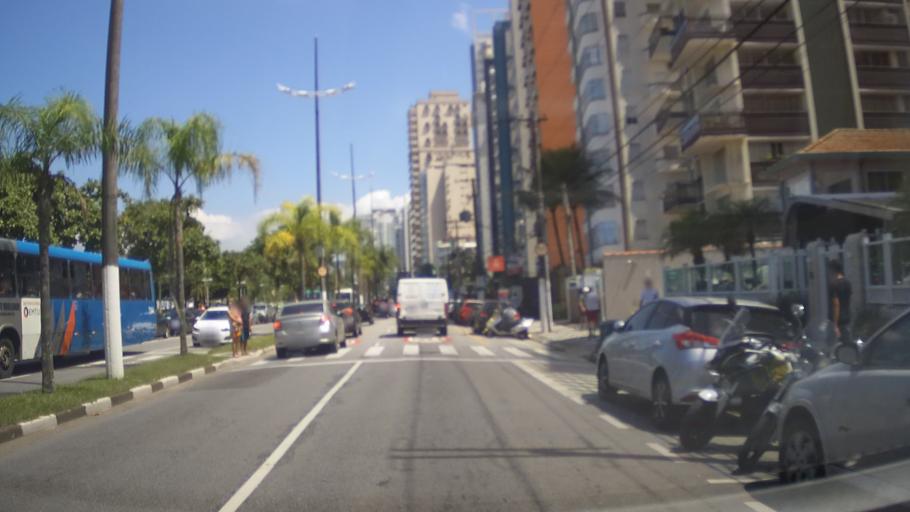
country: BR
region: Sao Paulo
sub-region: Santos
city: Santos
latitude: -23.9715
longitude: -46.3269
